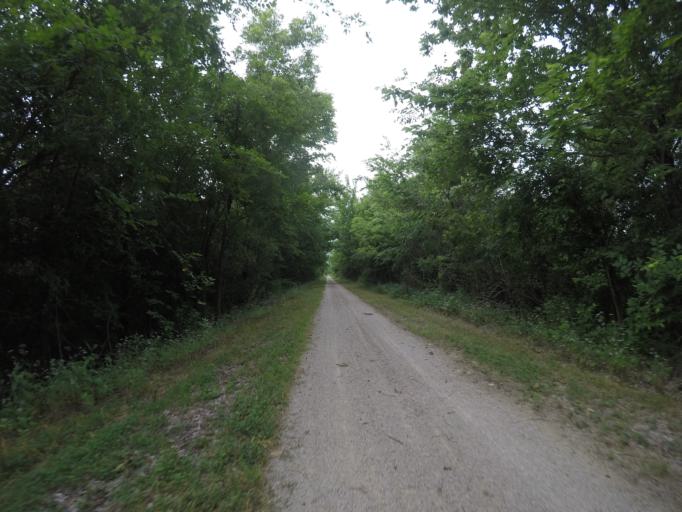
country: US
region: Kansas
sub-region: Franklin County
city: Ottawa
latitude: 38.5288
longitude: -95.2721
